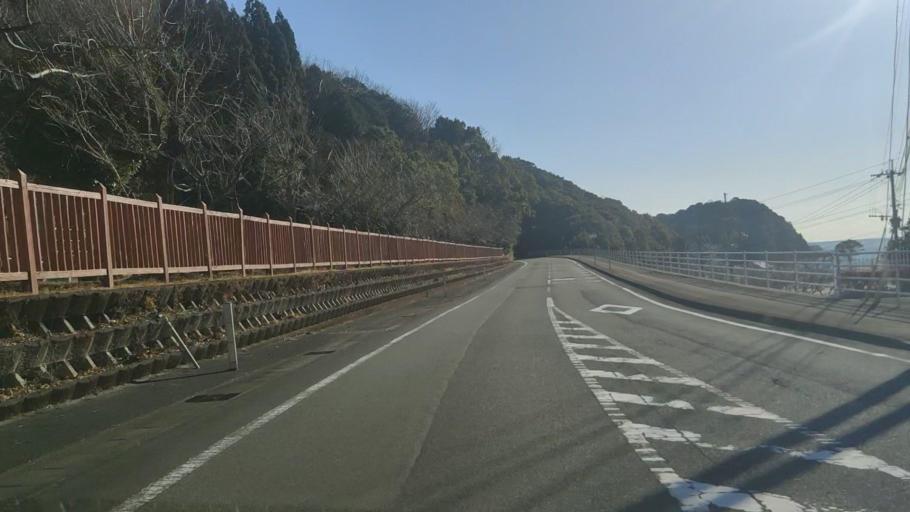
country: JP
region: Miyazaki
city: Nobeoka
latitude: 32.6624
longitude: 131.7610
